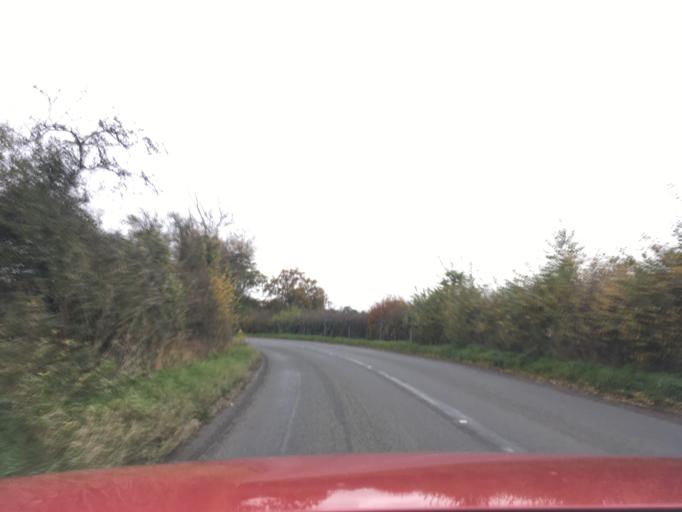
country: GB
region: England
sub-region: Dorset
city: Sherborne
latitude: 50.9895
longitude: -2.5736
